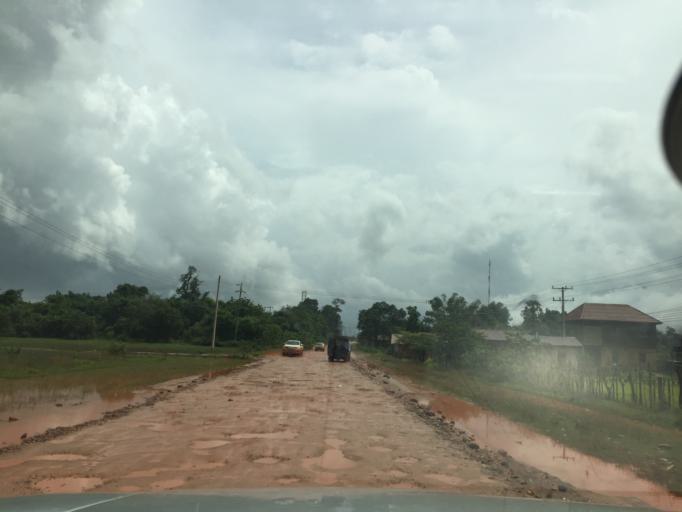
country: LA
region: Attapu
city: Attapu
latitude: 14.8150
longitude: 106.7870
